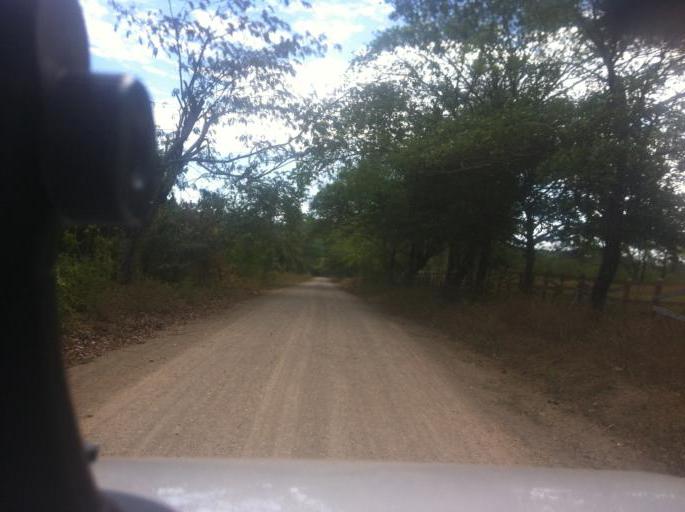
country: NI
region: Rivas
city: Belen
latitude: 11.5899
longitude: -86.0251
